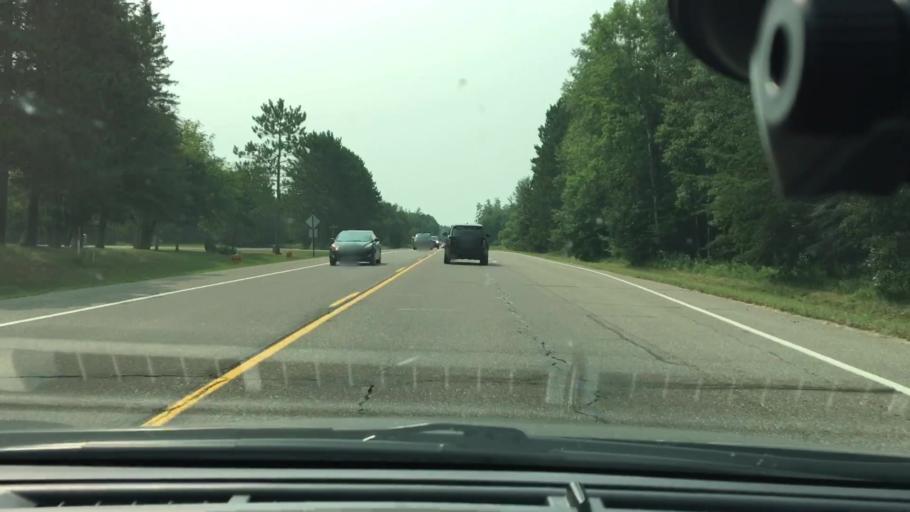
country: US
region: Minnesota
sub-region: Crow Wing County
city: Brainerd
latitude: 46.3949
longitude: -94.2234
